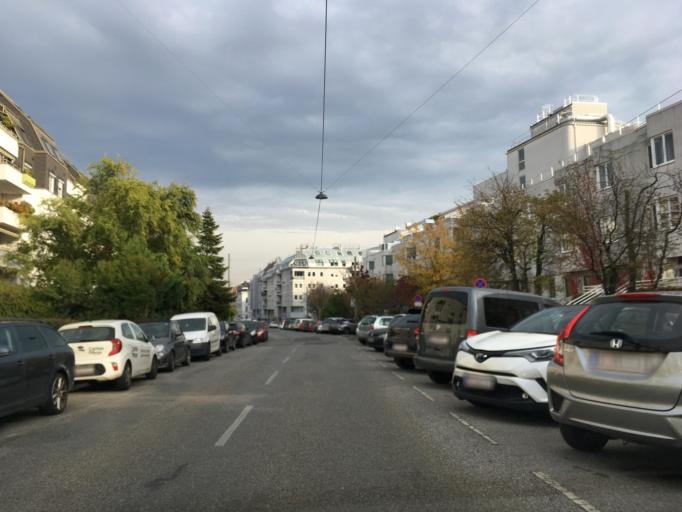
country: AT
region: Vienna
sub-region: Wien Stadt
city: Vienna
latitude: 48.2439
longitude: 16.3312
